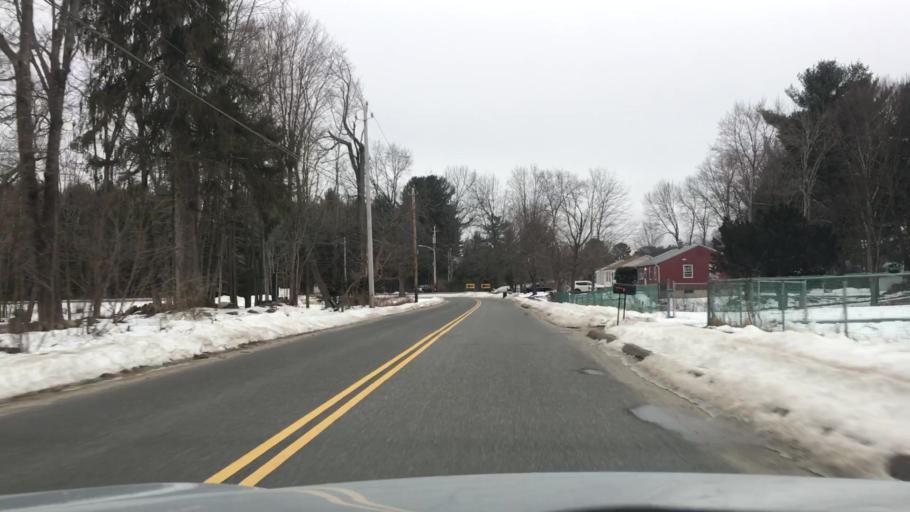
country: US
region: Massachusetts
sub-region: Hampshire County
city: Southampton
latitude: 42.1802
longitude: -72.6840
